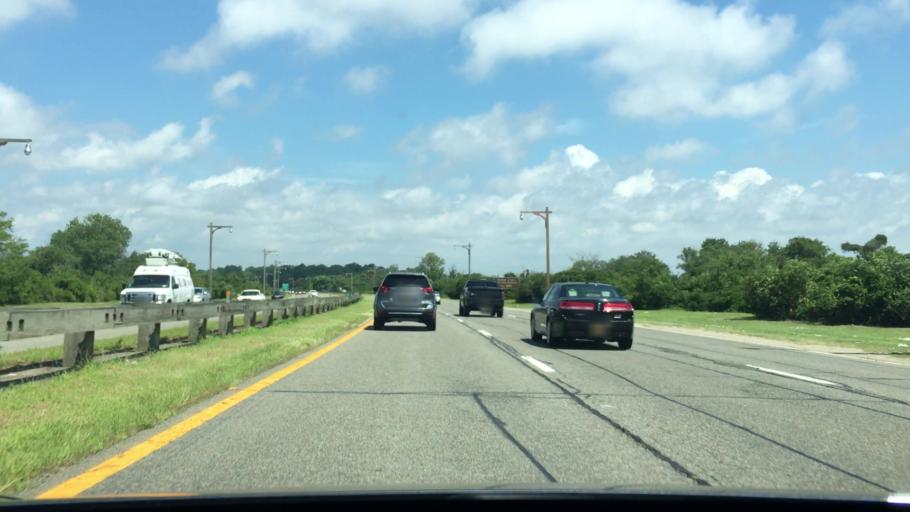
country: US
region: New York
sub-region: Nassau County
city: Merrick
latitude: 40.6321
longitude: -73.5620
